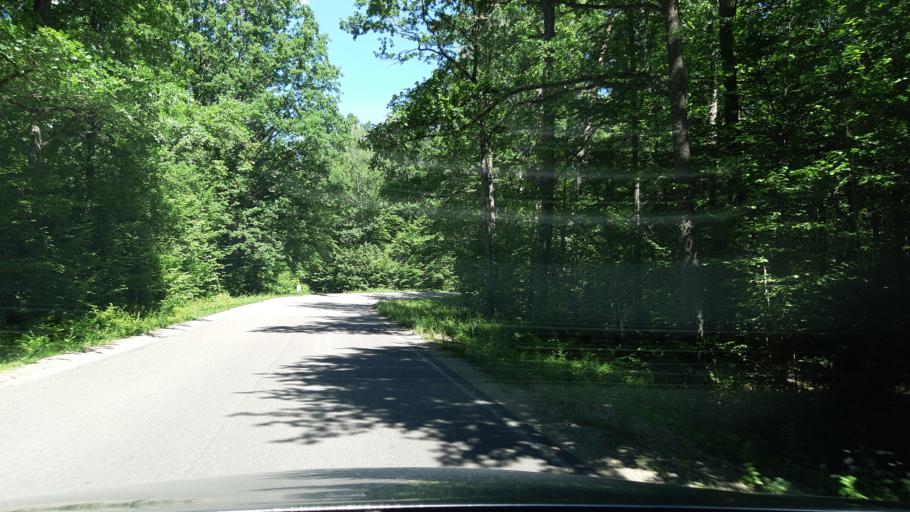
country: PL
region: Warmian-Masurian Voivodeship
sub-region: Powiat piski
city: Ruciane-Nida
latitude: 53.7218
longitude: 21.4962
